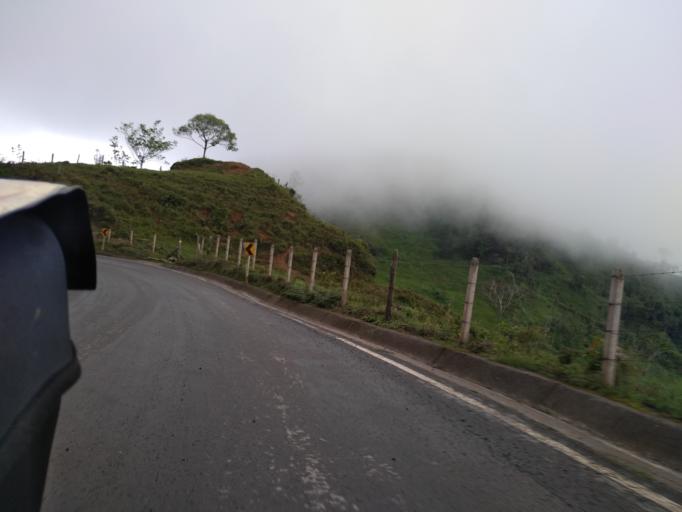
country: CO
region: Santander
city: Landazuri
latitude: 6.1865
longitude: -73.7183
